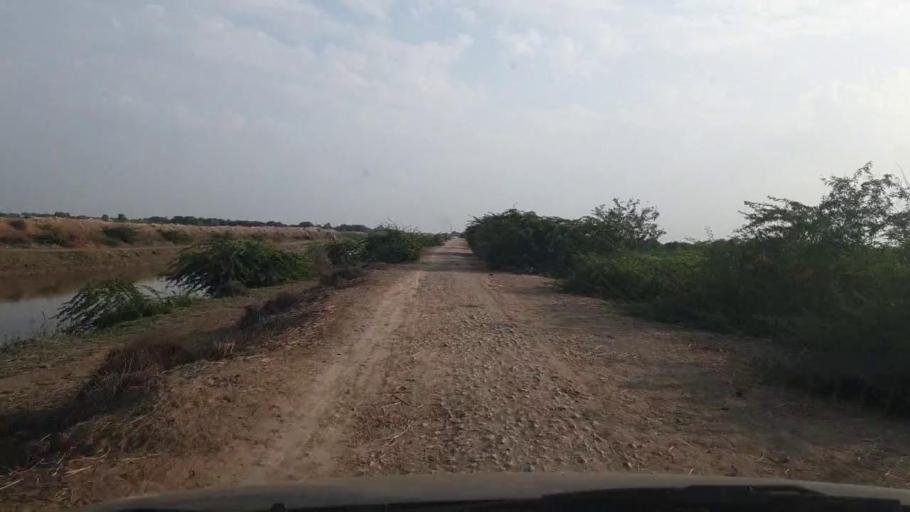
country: PK
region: Sindh
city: Badin
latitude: 24.5539
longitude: 68.6702
